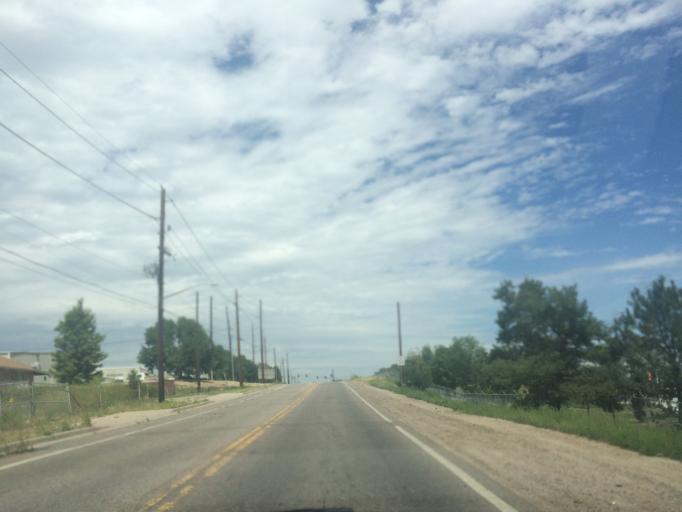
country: US
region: Colorado
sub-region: Adams County
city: Welby
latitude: 39.8138
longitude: -104.9592
